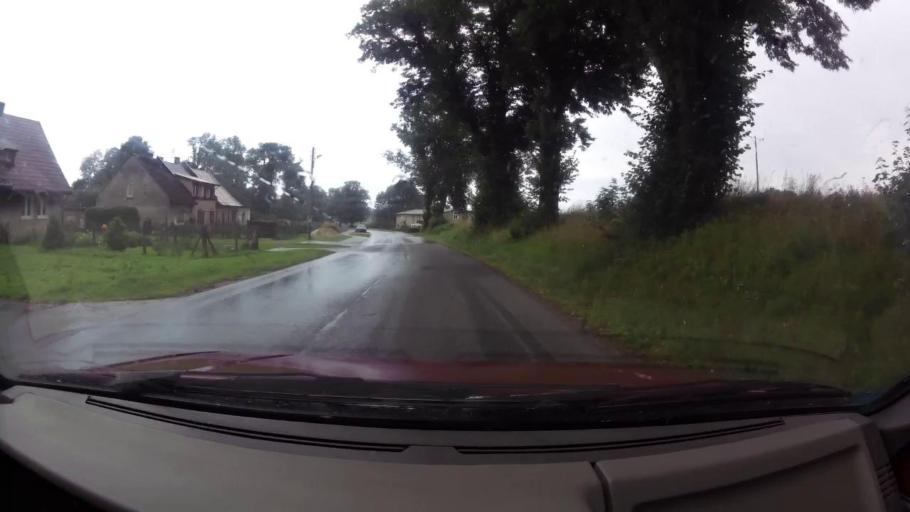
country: PL
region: West Pomeranian Voivodeship
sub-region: Koszalin
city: Koszalin
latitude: 54.1245
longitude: 16.1257
